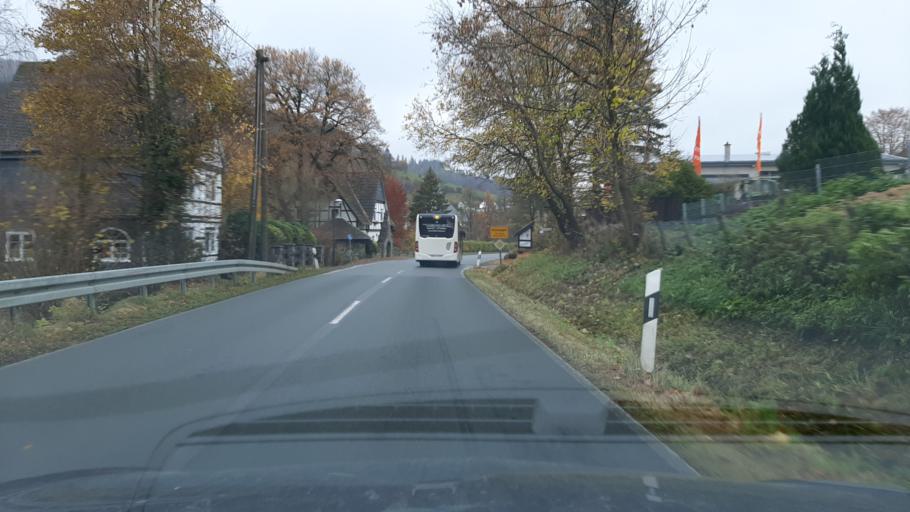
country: DE
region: North Rhine-Westphalia
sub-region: Regierungsbezirk Arnsberg
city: Olsberg
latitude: 51.2750
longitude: 8.4778
